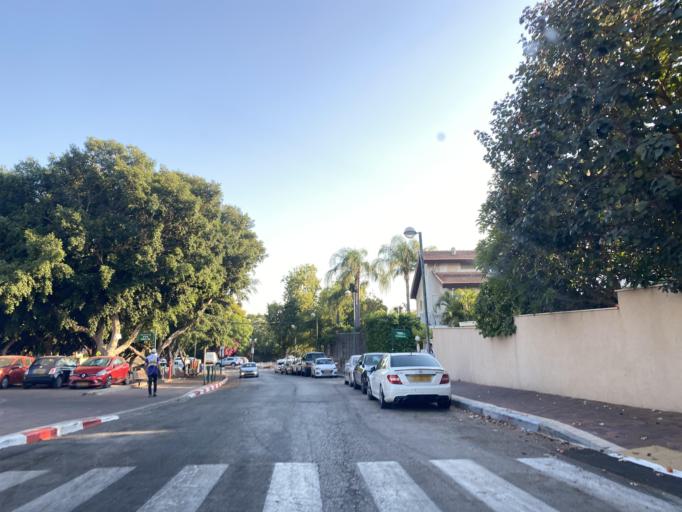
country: IL
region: Tel Aviv
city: Ramat HaSharon
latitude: 32.1412
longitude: 34.8444
